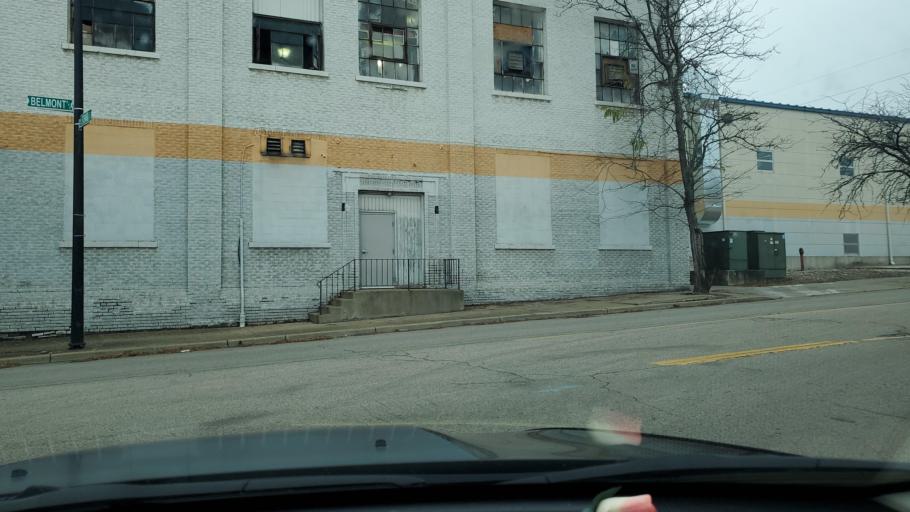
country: US
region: Ohio
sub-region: Mahoning County
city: Youngstown
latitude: 41.1059
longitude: -80.6556
